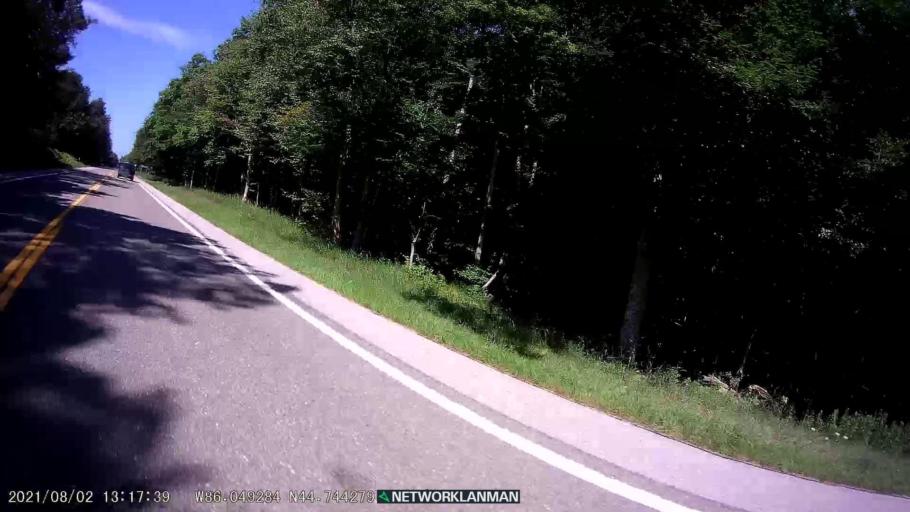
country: US
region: Michigan
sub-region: Benzie County
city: Beulah
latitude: 44.7444
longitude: -86.0492
